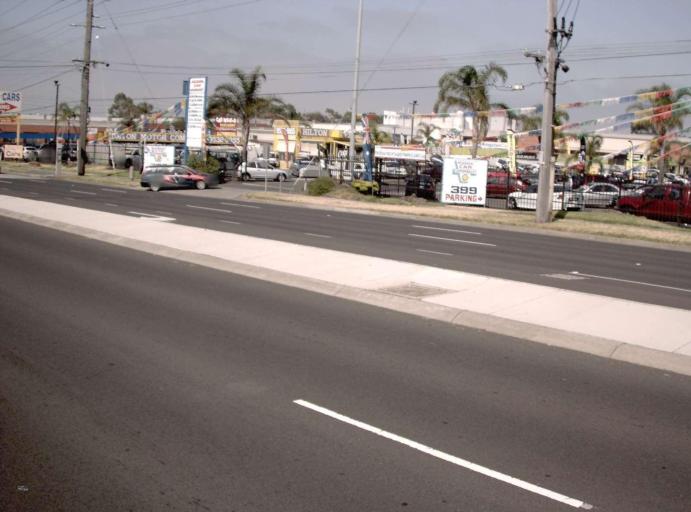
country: AU
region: Victoria
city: Heatherton
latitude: -37.9520
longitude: 145.0771
